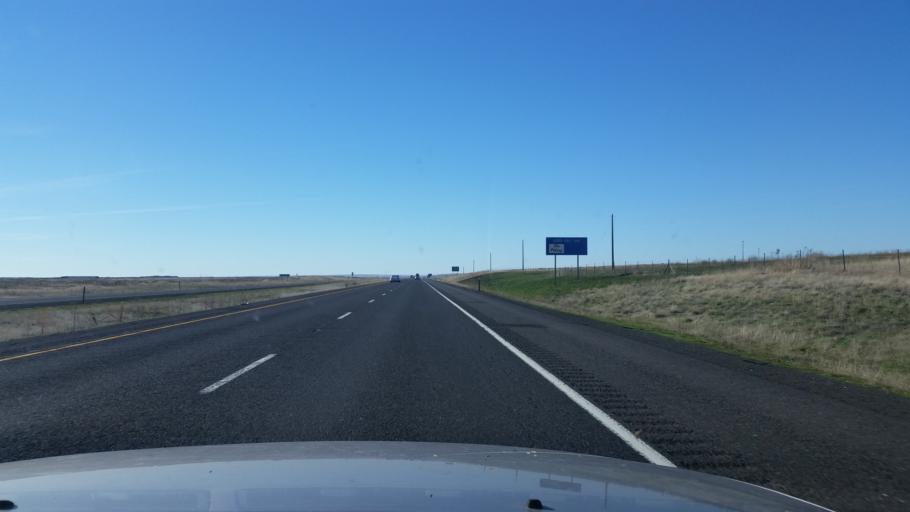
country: US
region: Washington
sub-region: Spokane County
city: Medical Lake
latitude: 47.3169
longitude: -117.9544
